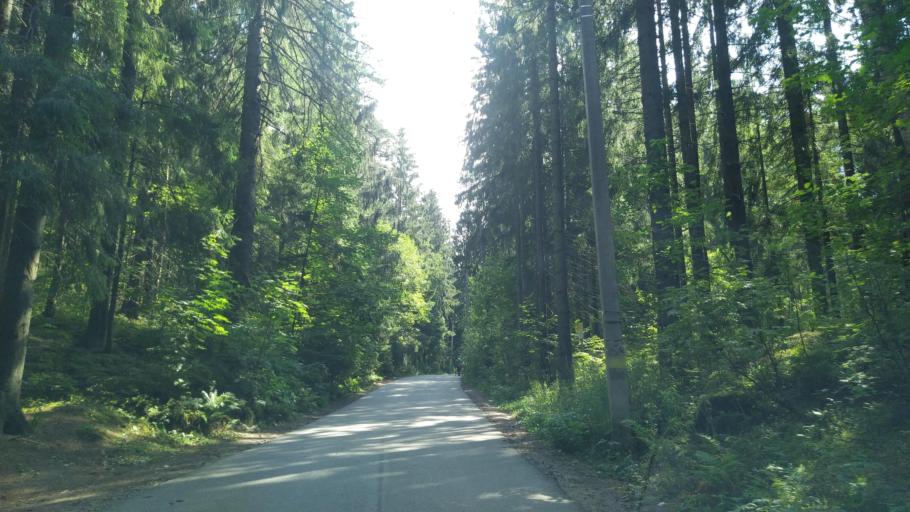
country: RU
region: Leningrad
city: Toksovo
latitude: 60.1703
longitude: 30.5324
